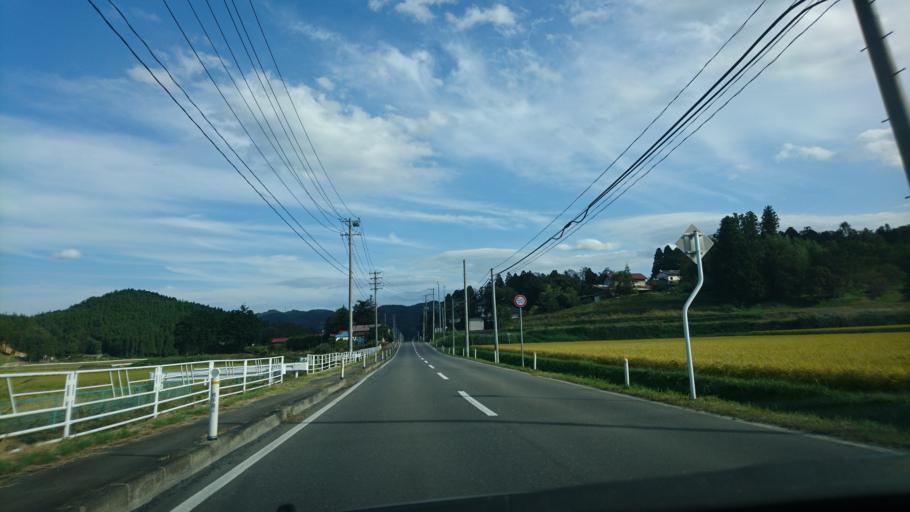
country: JP
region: Iwate
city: Ichinoseki
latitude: 38.8370
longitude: 141.2384
